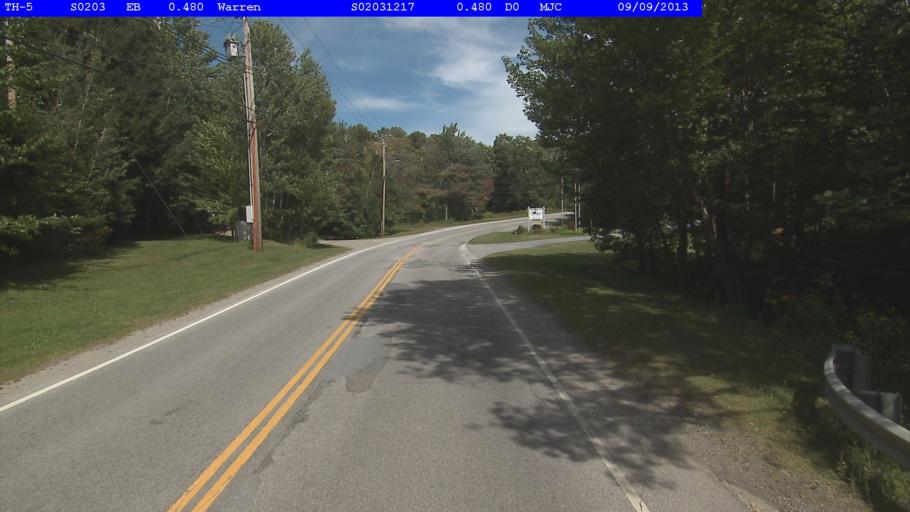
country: US
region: Vermont
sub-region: Addison County
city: Bristol
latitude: 44.1381
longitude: -72.8869
